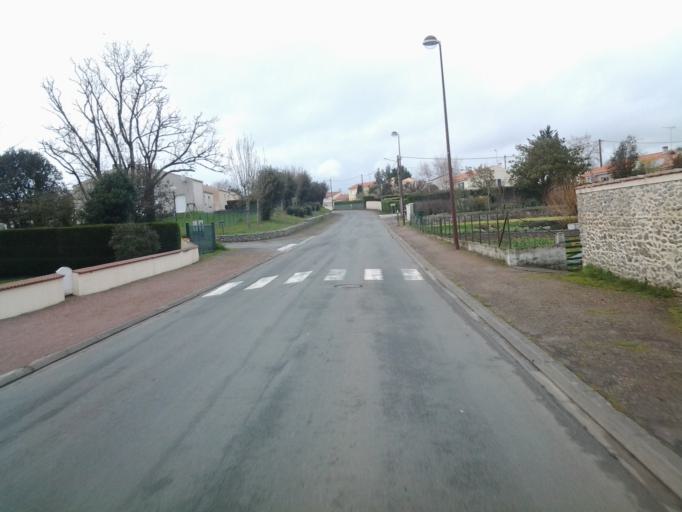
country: FR
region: Pays de la Loire
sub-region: Departement de la Vendee
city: Avrille
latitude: 46.4653
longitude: -1.4897
